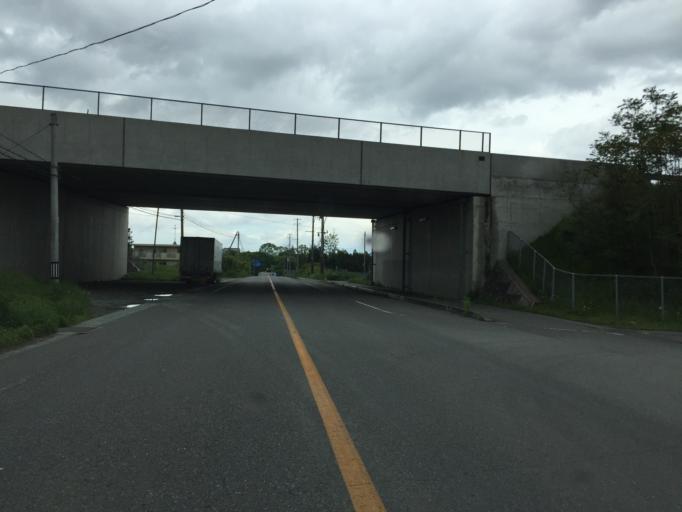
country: JP
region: Fukushima
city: Sukagawa
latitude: 37.1929
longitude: 140.3408
